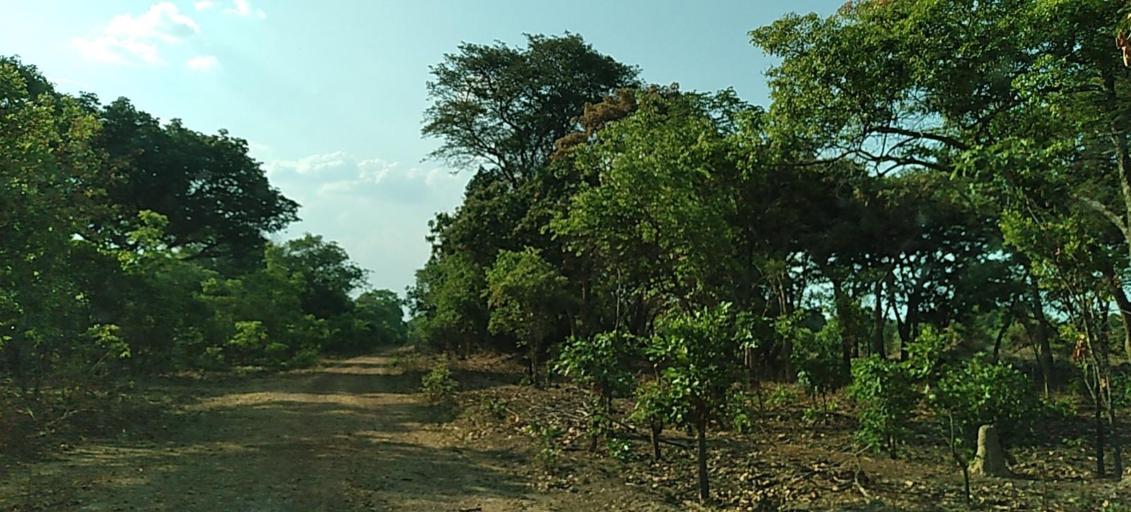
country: ZM
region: Copperbelt
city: Mpongwe
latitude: -13.3934
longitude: 28.0153
